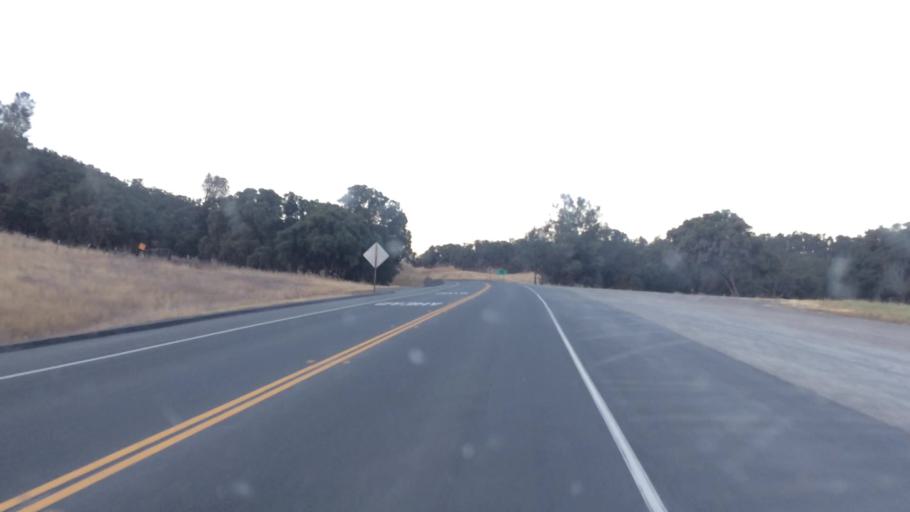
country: US
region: California
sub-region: Amador County
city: Plymouth
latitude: 38.4522
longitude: -120.8730
